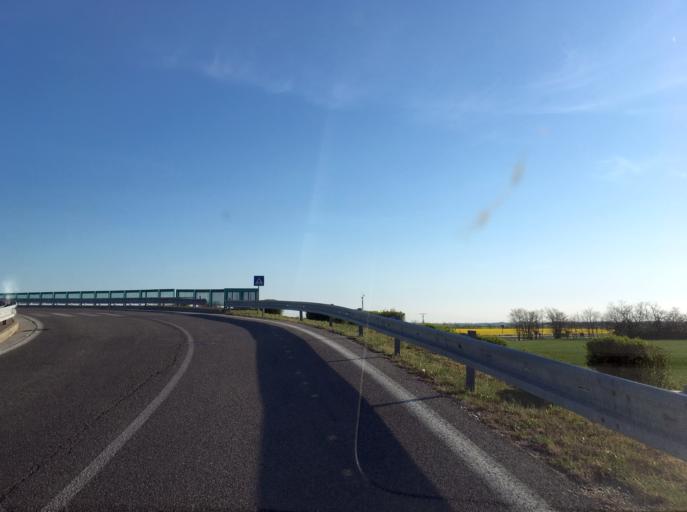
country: AT
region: Burgenland
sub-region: Politischer Bezirk Neusiedl am See
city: Kittsee
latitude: 48.0708
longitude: 17.0907
